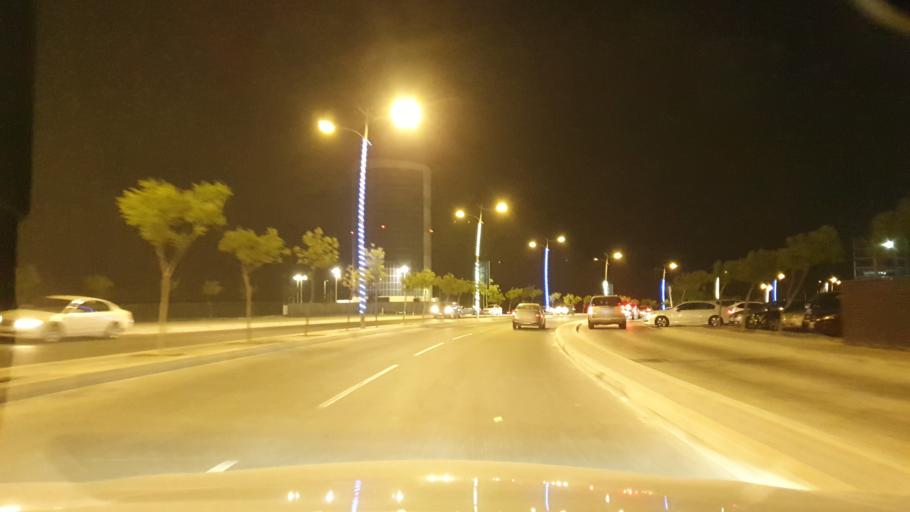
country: BH
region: Manama
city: Jidd Hafs
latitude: 26.2421
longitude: 50.5522
